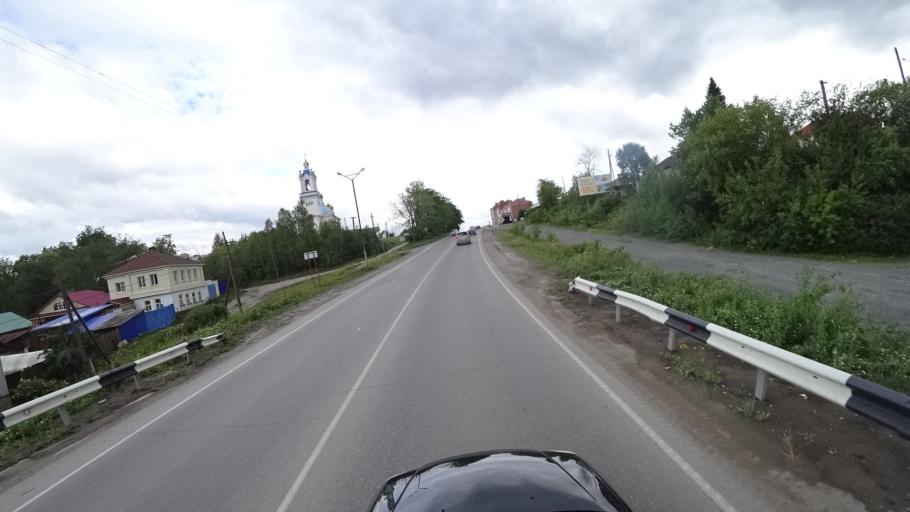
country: RU
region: Sverdlovsk
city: Kamyshlov
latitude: 56.8462
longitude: 62.6864
